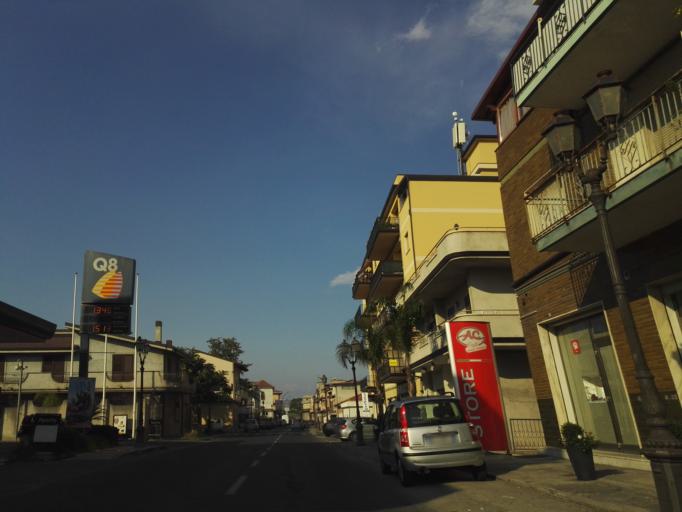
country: IT
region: Calabria
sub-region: Provincia di Reggio Calabria
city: Siderno
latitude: 38.2730
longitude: 16.3033
